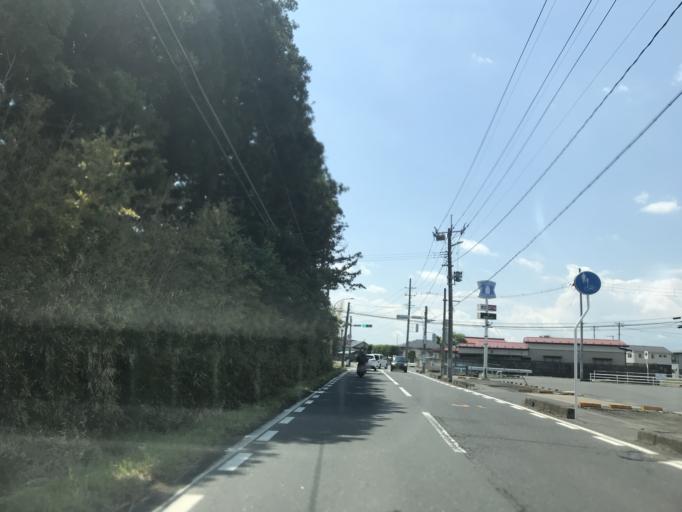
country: JP
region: Miyagi
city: Kogota
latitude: 38.5773
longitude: 141.0332
